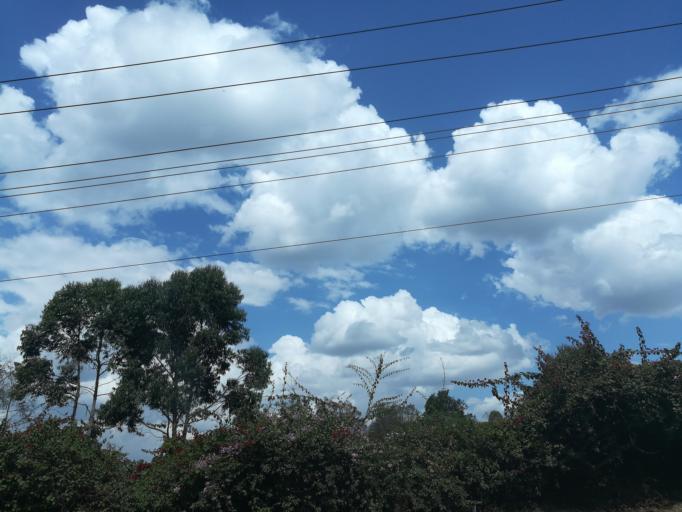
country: KE
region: Nairobi Area
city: Nairobi
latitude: -1.3284
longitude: 36.7897
